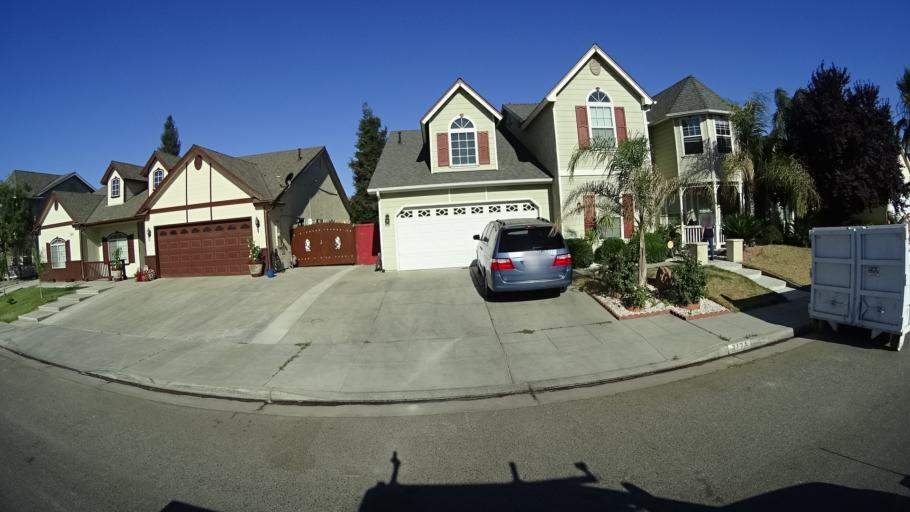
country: US
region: California
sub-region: Fresno County
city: West Park
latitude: 36.7812
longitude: -119.8664
